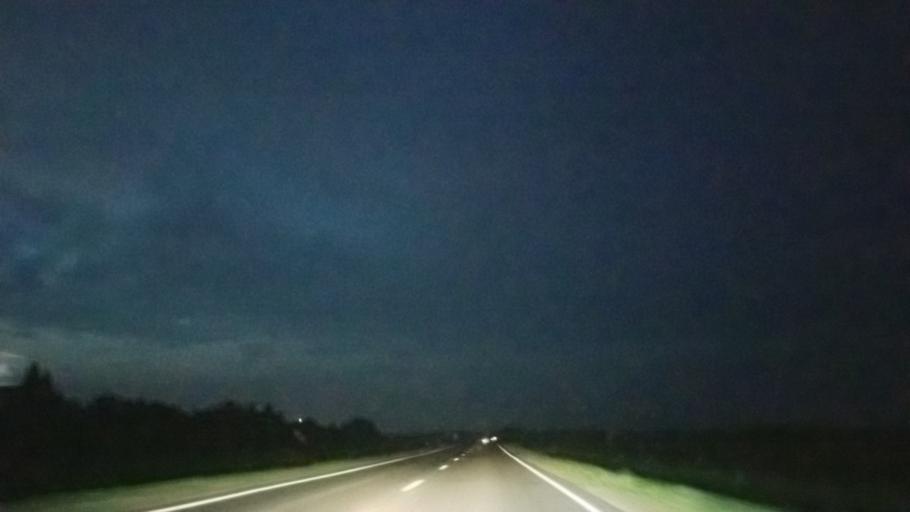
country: BY
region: Brest
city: Brest
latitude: 51.9957
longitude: 23.7105
